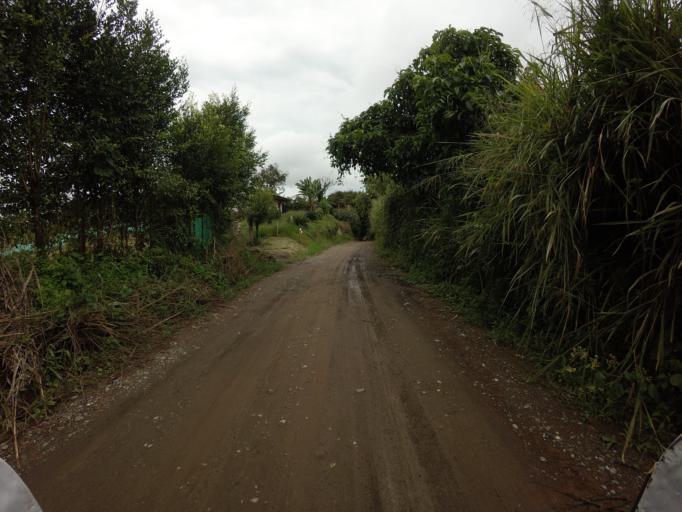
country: CO
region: Valle del Cauca
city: Ulloa
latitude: 4.6977
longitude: -75.7306
